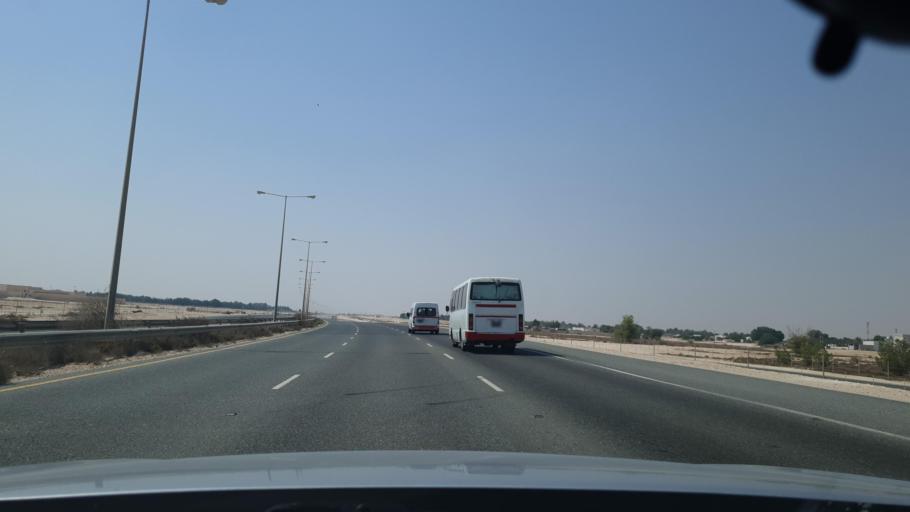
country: QA
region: Al Khawr
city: Al Khawr
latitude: 25.7577
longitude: 51.4645
